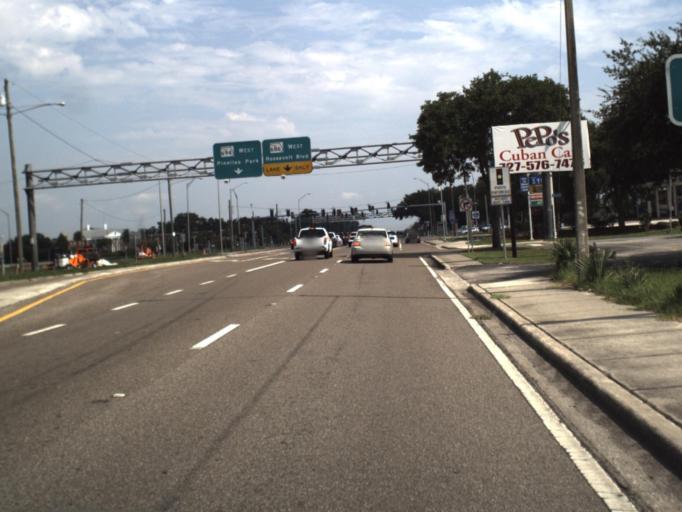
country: US
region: Florida
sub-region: Pinellas County
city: Gandy
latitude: 27.8628
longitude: -82.6387
